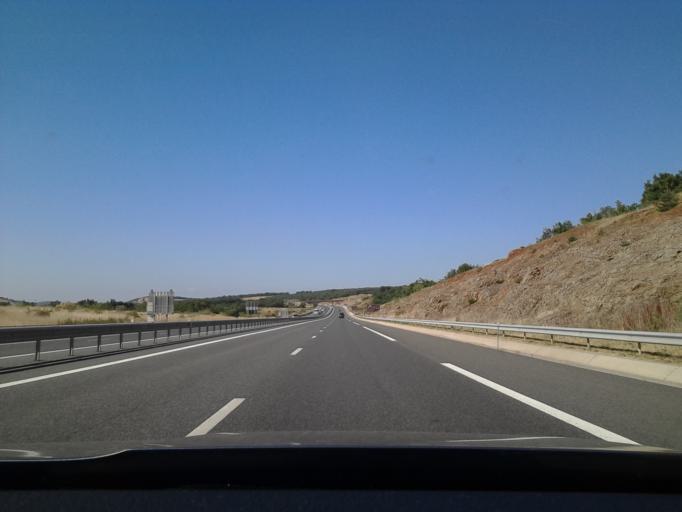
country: FR
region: Midi-Pyrenees
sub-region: Departement de l'Aveyron
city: Creissels
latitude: 44.1603
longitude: 3.0246
